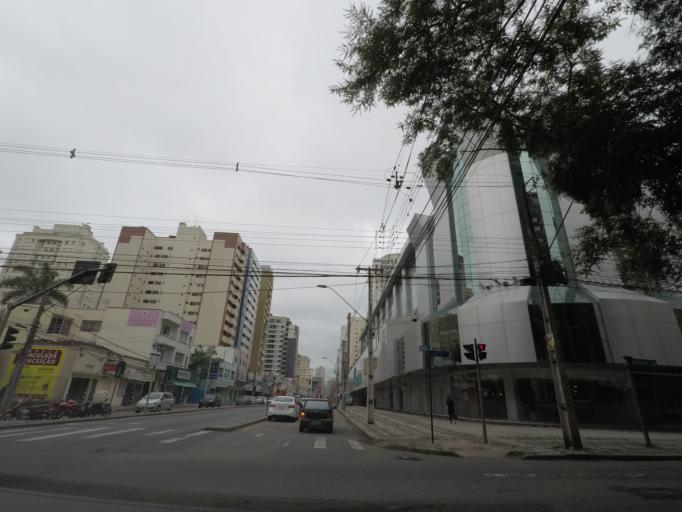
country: BR
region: Parana
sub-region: Curitiba
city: Curitiba
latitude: -25.4538
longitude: -49.2880
